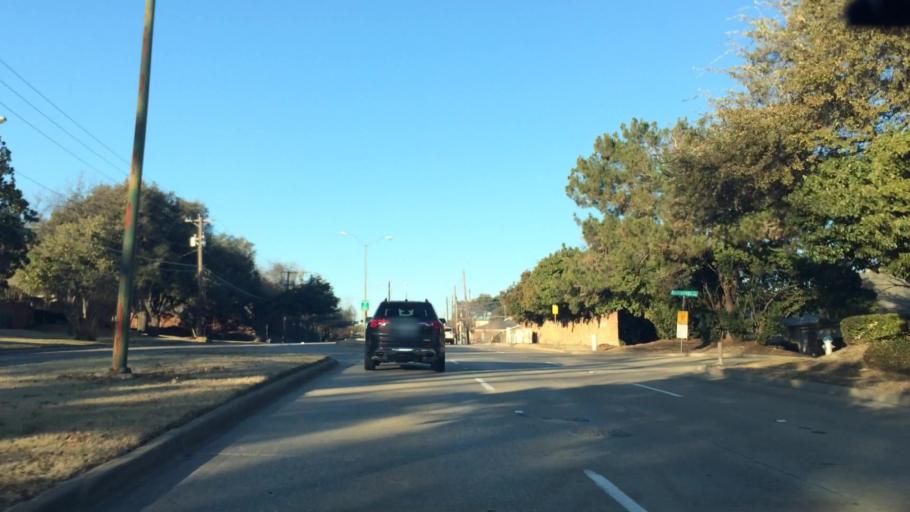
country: US
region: Texas
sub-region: Dallas County
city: Addison
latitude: 32.9387
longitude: -96.8012
